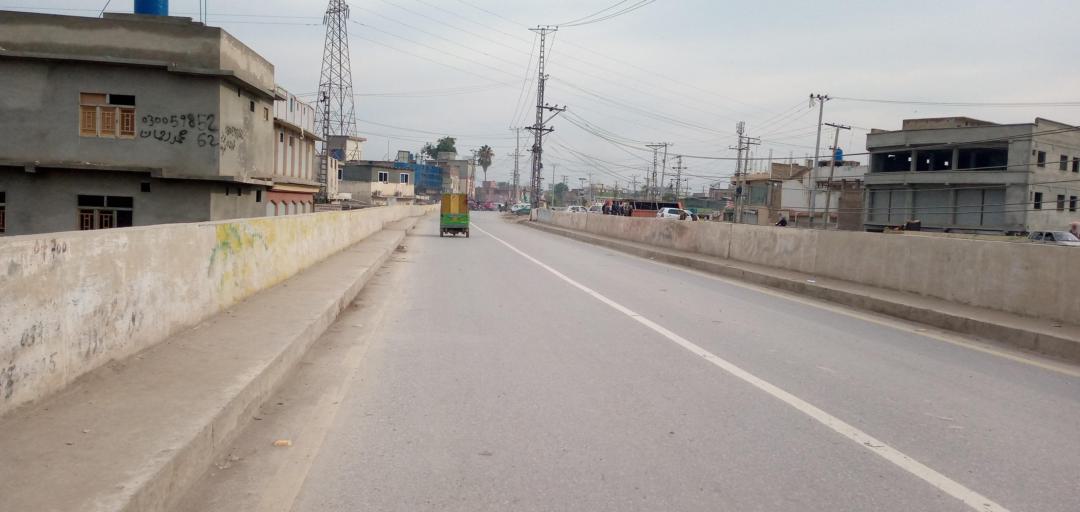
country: PK
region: Khyber Pakhtunkhwa
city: Peshawar
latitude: 34.0039
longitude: 71.4665
